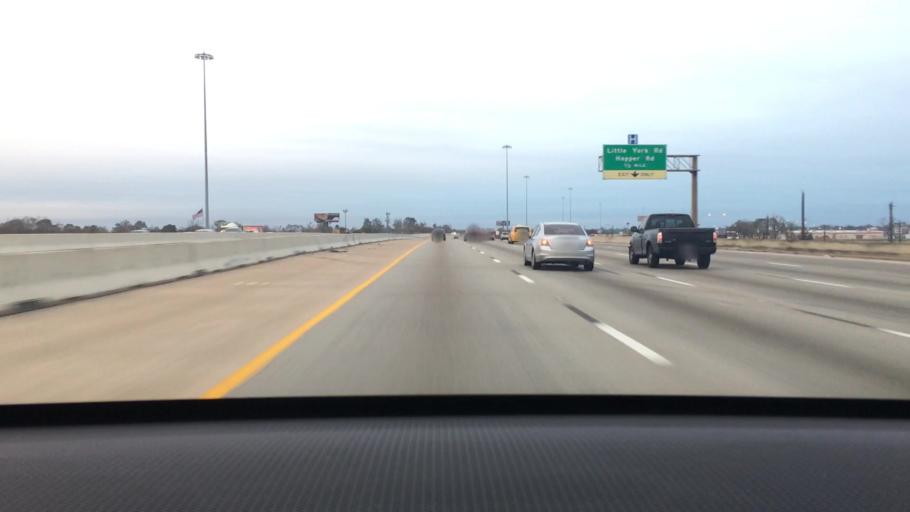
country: US
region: Texas
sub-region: Harris County
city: Aldine
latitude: 29.8593
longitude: -95.3334
